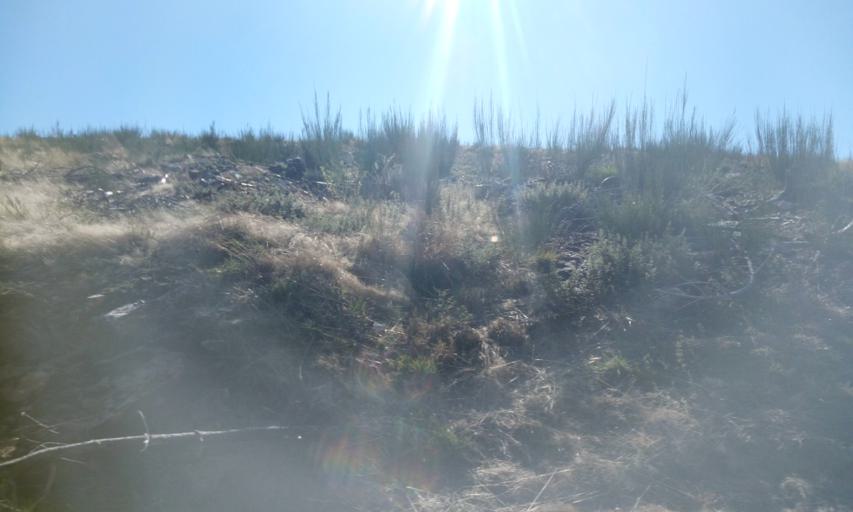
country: PT
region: Guarda
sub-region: Manteigas
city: Manteigas
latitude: 40.4965
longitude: -7.5330
